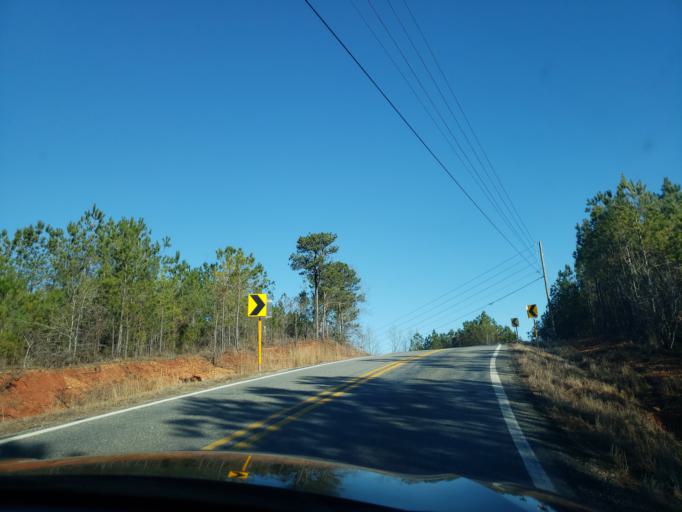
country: US
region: Alabama
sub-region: Elmore County
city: Tallassee
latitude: 32.6719
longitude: -85.8916
